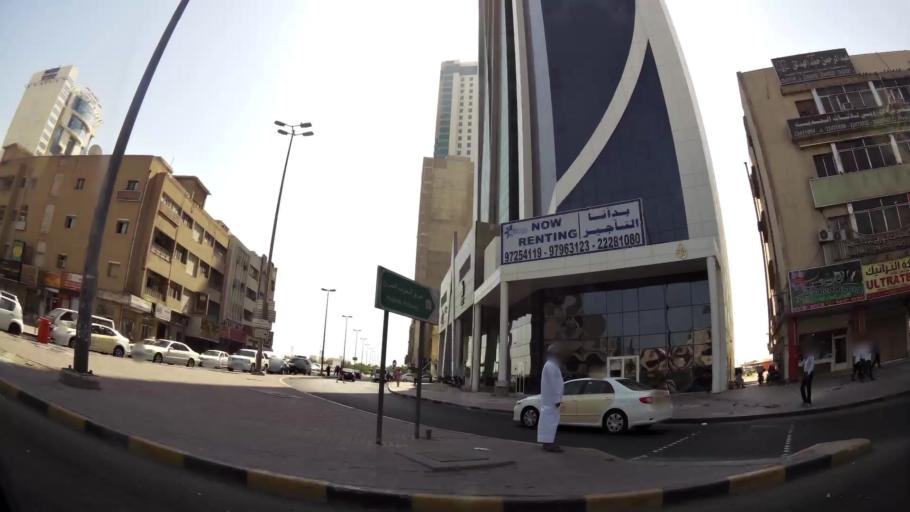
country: KW
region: Al Asimah
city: Kuwait City
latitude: 29.3693
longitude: 47.9795
